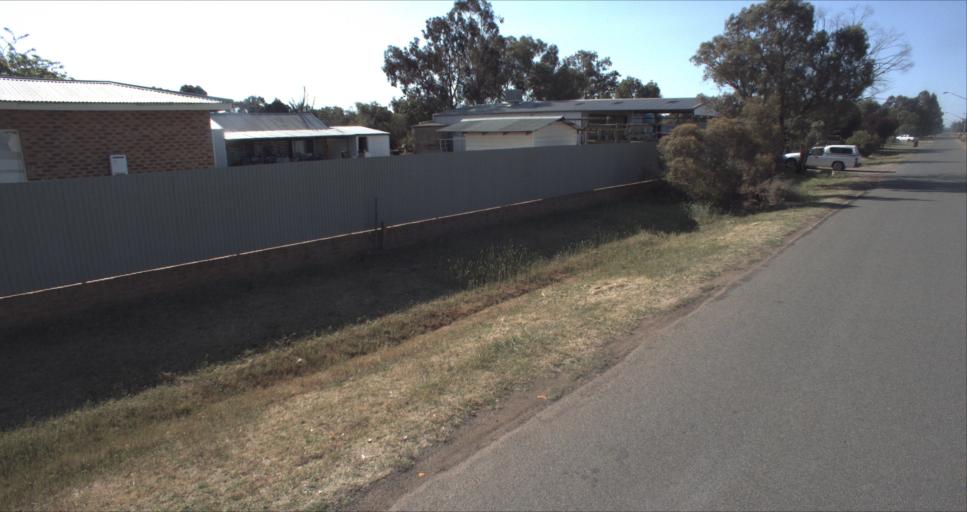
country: AU
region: New South Wales
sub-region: Leeton
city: Leeton
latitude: -34.5497
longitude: 146.4139
